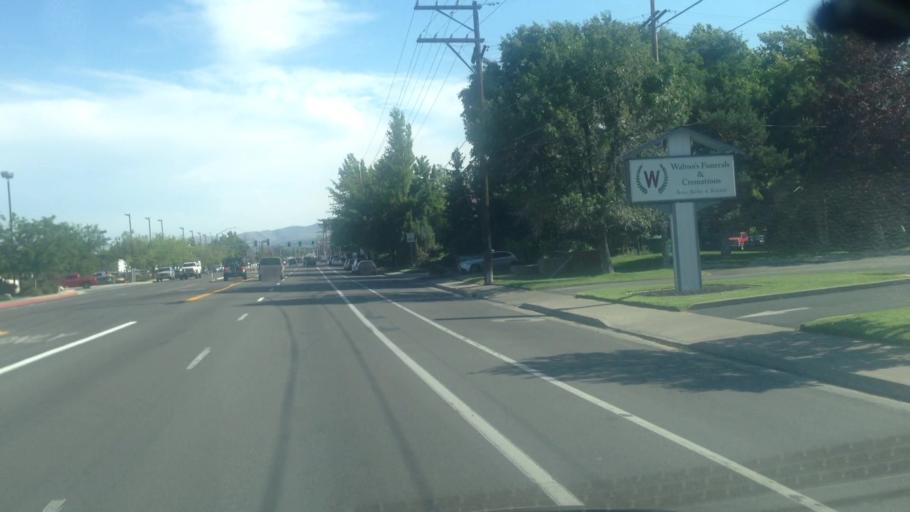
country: US
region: Nevada
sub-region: Washoe County
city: Reno
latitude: 39.5032
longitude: -119.7892
